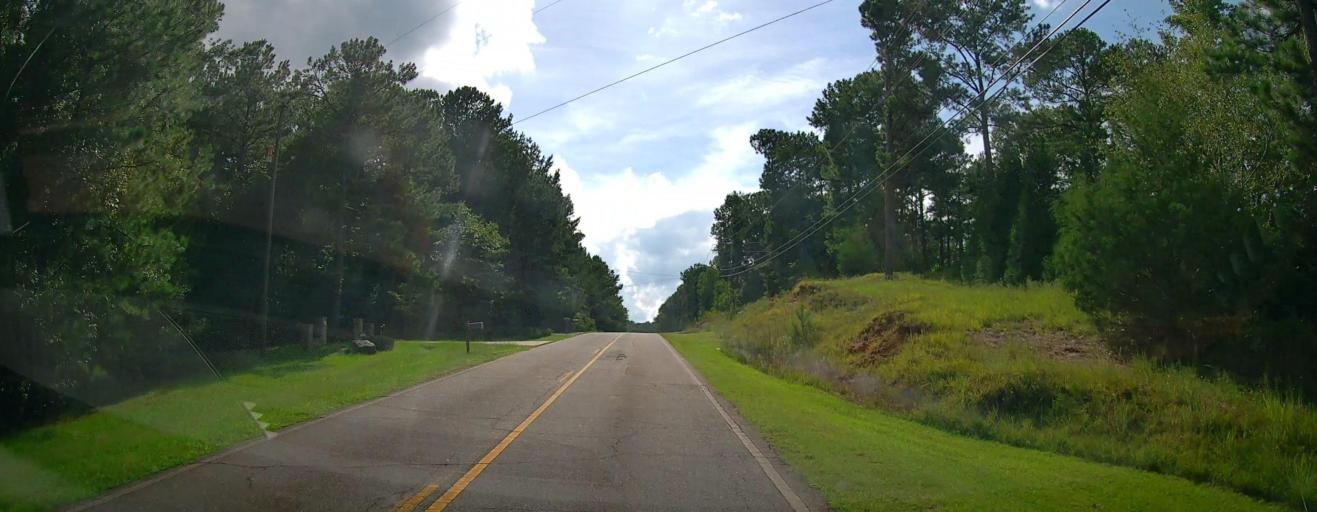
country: US
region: Alabama
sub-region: Russell County
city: Phenix City
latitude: 32.6069
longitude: -84.9680
